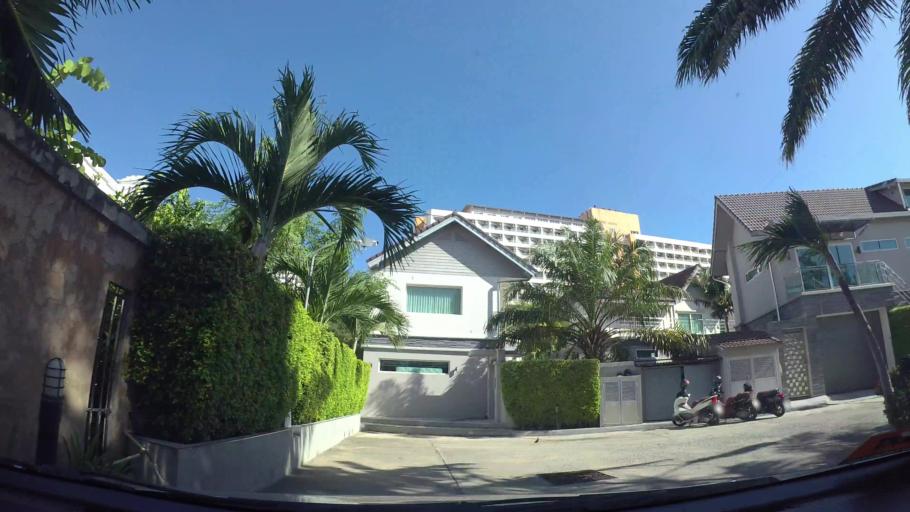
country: TH
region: Chon Buri
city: Phatthaya
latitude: 12.9067
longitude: 100.8728
